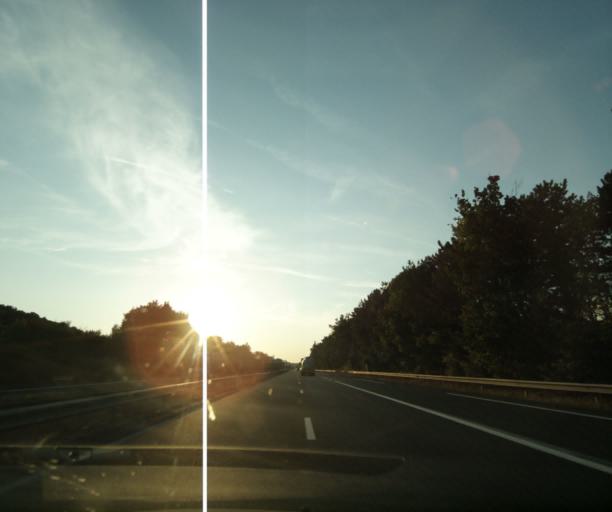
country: FR
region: Aquitaine
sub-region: Departement du Lot-et-Garonne
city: Boe
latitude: 44.1629
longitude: 0.6012
